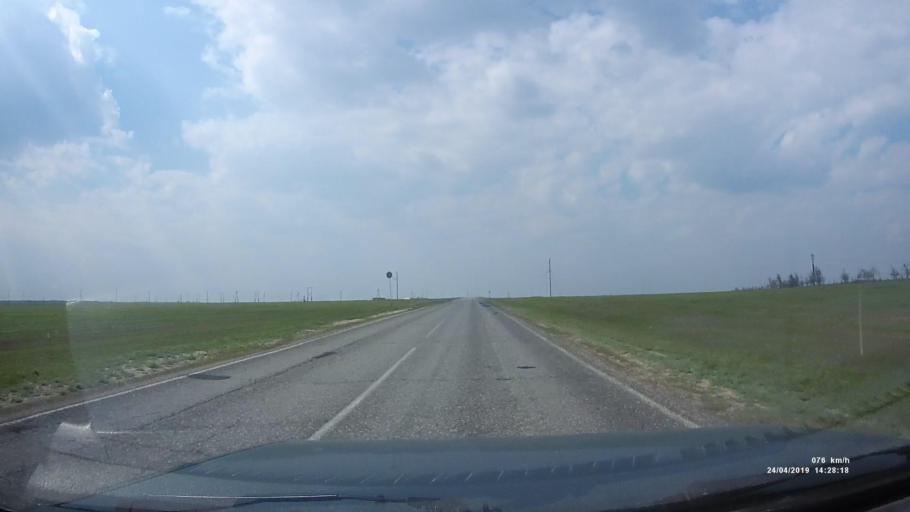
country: RU
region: Kalmykiya
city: Arshan'
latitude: 46.3382
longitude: 44.0318
